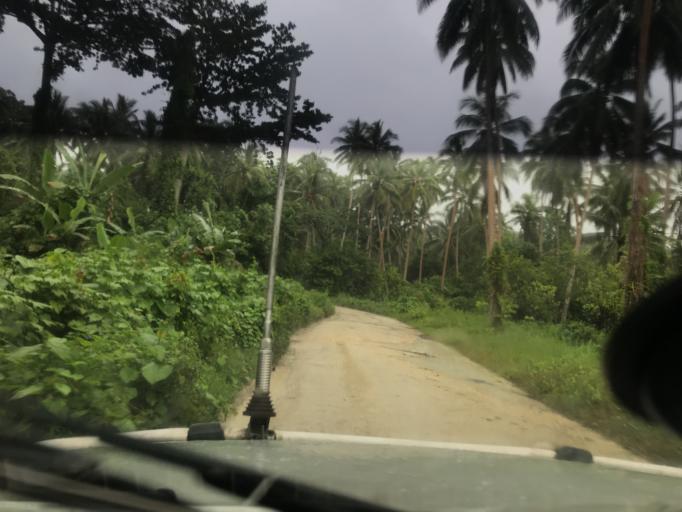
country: SB
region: Malaita
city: Auki
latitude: -9.0700
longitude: 160.8107
